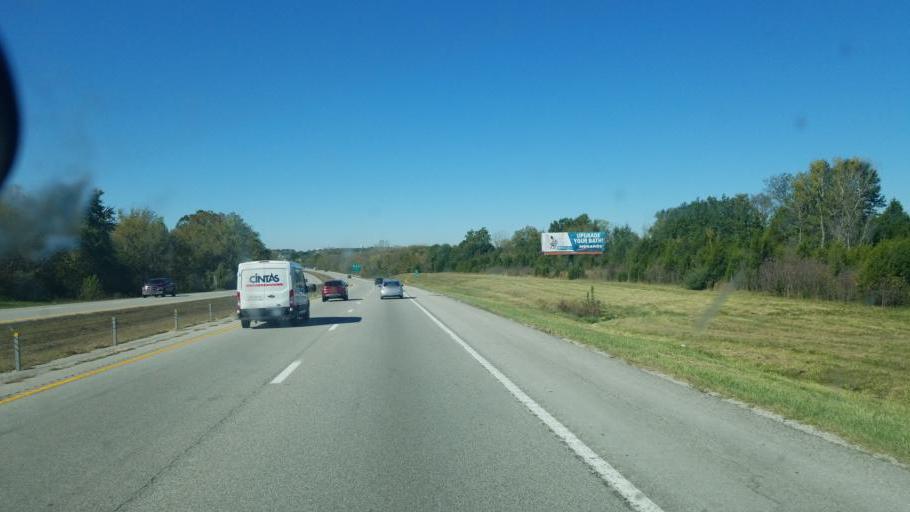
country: US
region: Missouri
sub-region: Jackson County
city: Grain Valley
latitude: 39.0196
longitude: -94.1709
